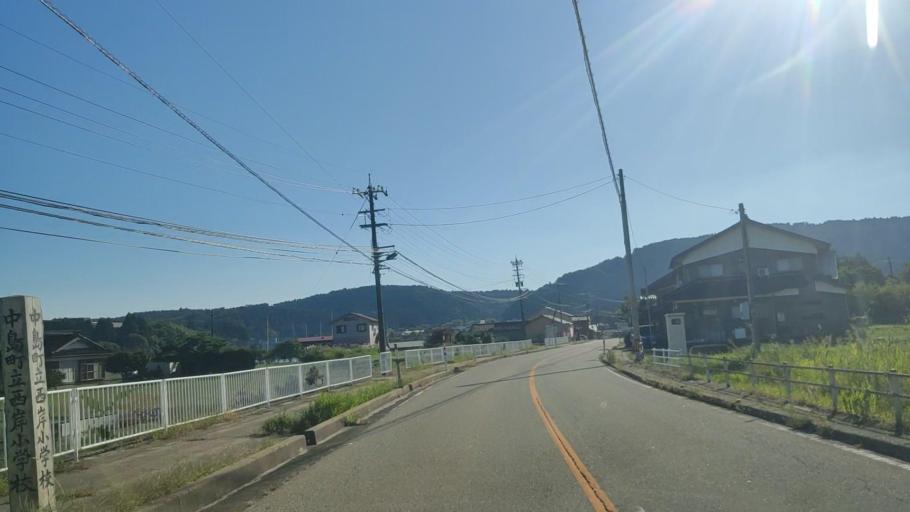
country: JP
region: Ishikawa
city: Nanao
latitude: 37.1484
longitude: 136.8760
